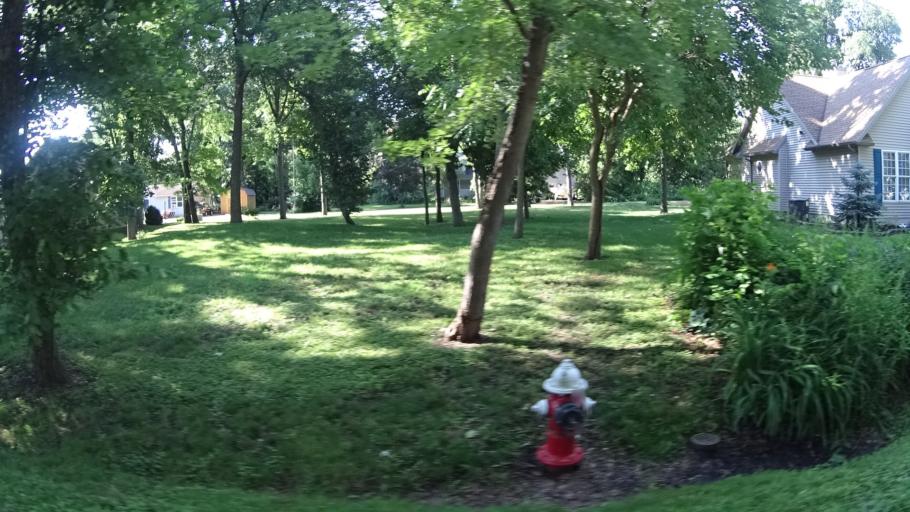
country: US
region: Ohio
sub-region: Erie County
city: Sandusky
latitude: 41.4652
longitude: -82.8241
